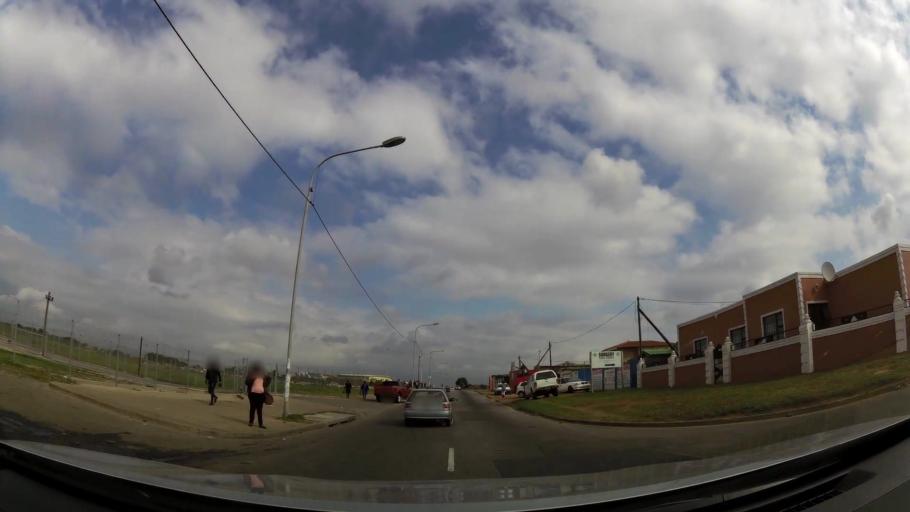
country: ZA
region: Eastern Cape
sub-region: Nelson Mandela Bay Metropolitan Municipality
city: Port Elizabeth
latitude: -33.8103
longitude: 25.5931
